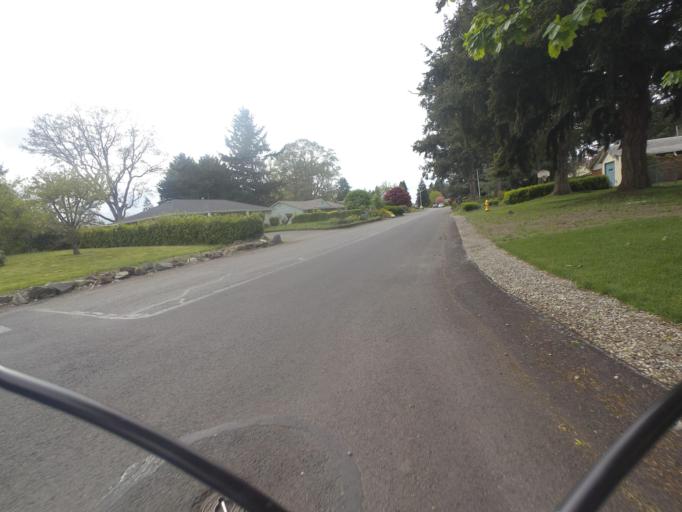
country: US
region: Washington
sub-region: Pierce County
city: McChord Air Force Base
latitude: 47.1614
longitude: -122.4870
